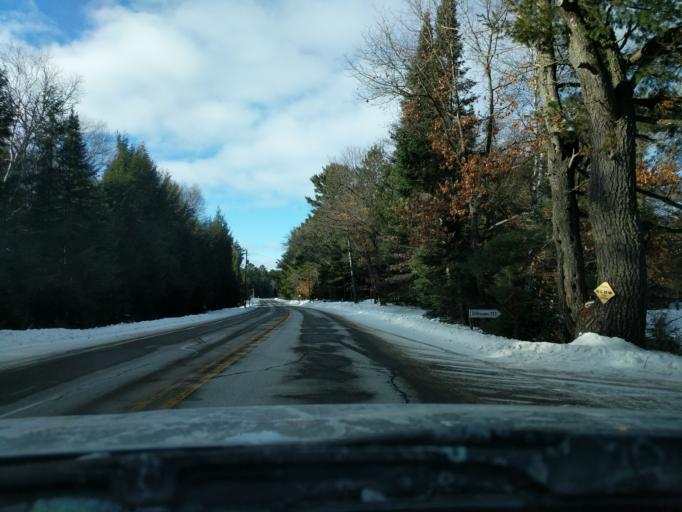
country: US
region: Wisconsin
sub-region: Vilas County
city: Eagle River
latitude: 45.7711
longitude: -89.0679
